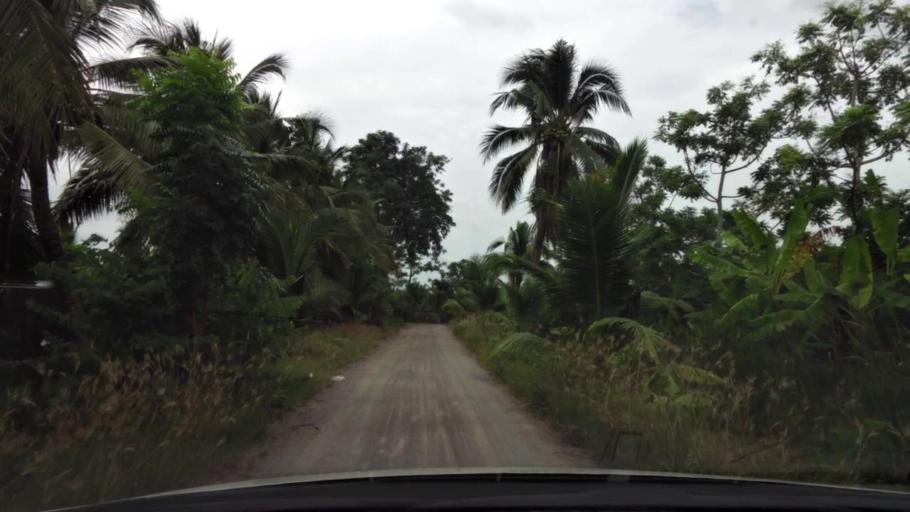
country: TH
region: Ratchaburi
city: Damnoen Saduak
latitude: 13.5652
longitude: 100.0044
